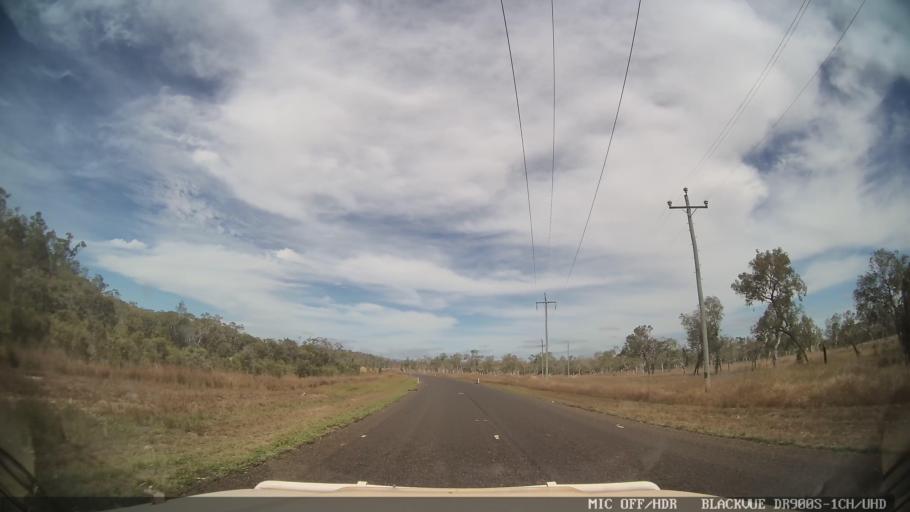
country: AU
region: Queensland
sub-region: Tablelands
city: Mareeba
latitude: -16.8495
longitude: 145.3823
